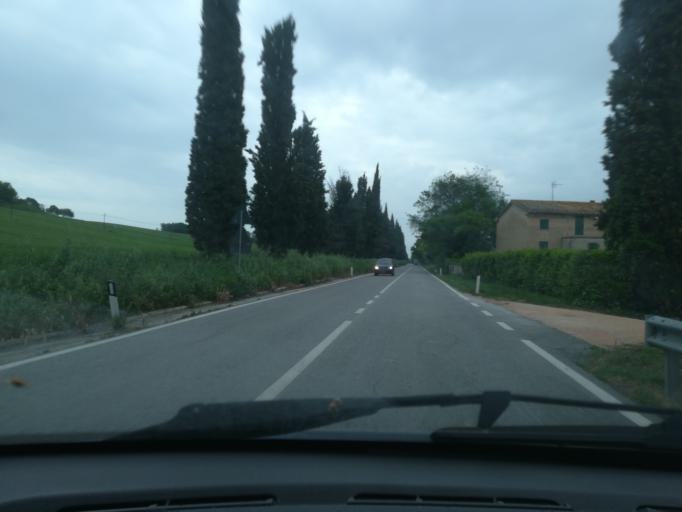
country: IT
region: The Marches
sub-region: Provincia di Macerata
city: Treia
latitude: 43.2746
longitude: 13.2929
